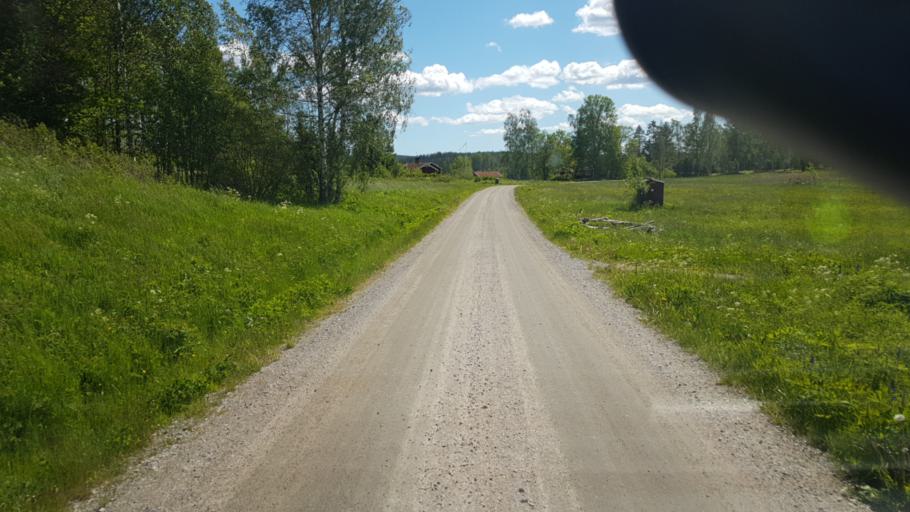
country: SE
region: Vaermland
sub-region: Karlstads Kommun
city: Edsvalla
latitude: 59.6016
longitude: 12.9198
